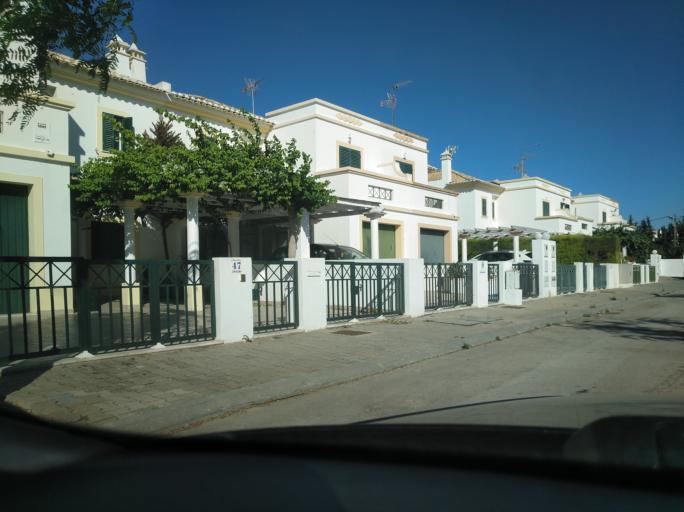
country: PT
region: Faro
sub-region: Vila Real de Santo Antonio
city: Monte Gordo
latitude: 37.1699
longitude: -7.5161
